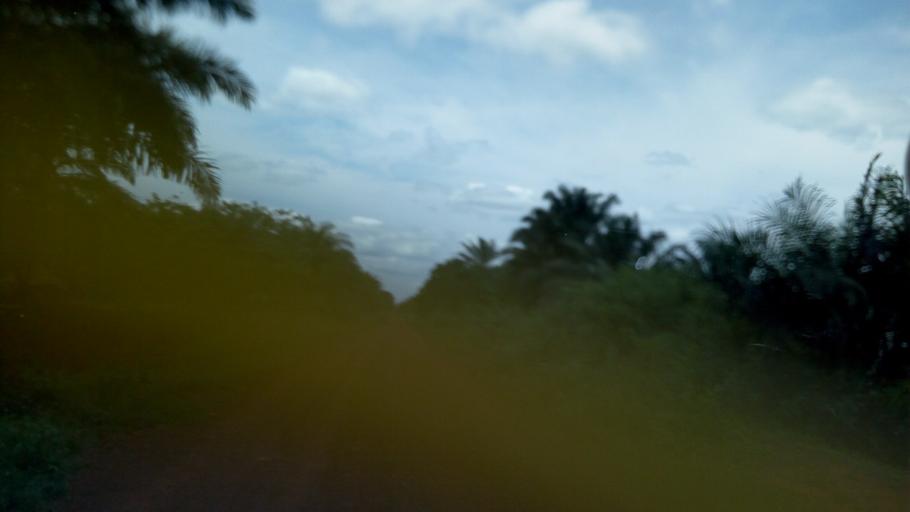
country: CD
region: Equateur
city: Gemena
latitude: 3.5244
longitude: 19.3621
